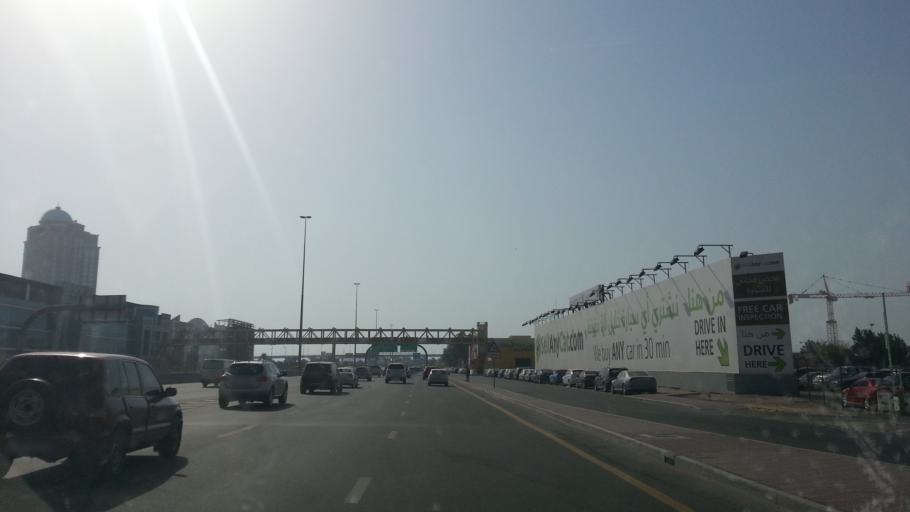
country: AE
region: Dubai
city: Dubai
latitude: 25.1183
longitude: 55.2094
